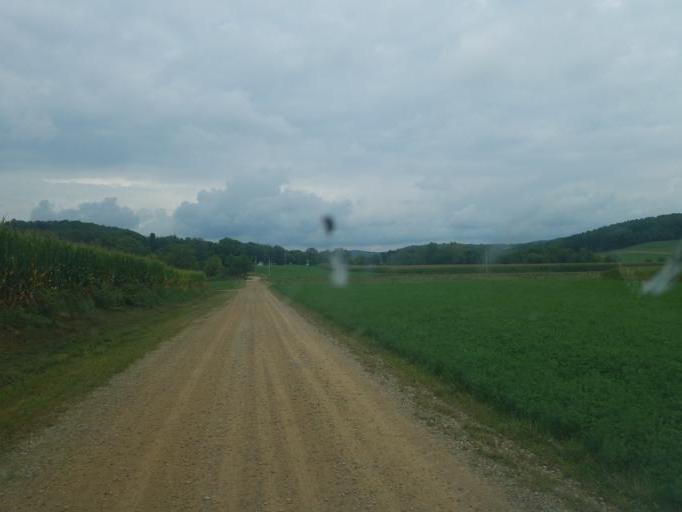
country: US
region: Ohio
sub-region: Knox County
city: Danville
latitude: 40.5270
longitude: -82.3050
